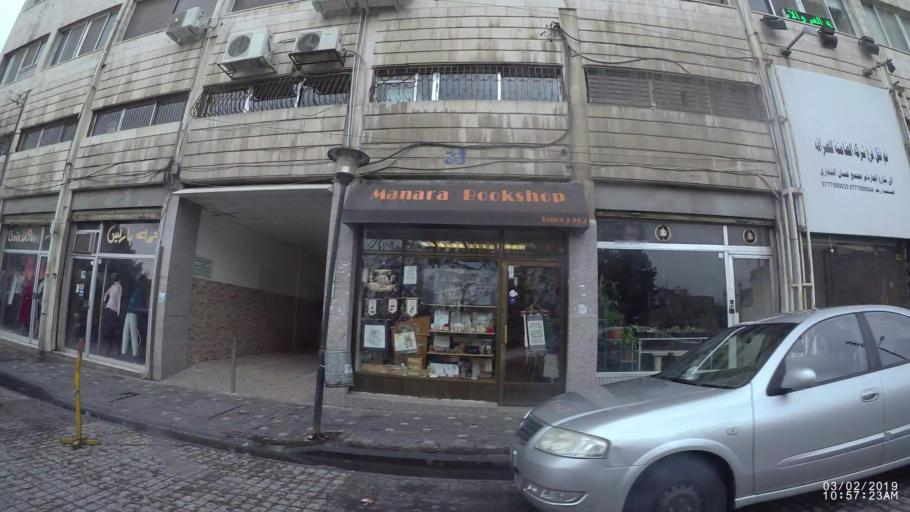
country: JO
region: Amman
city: Amman
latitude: 31.9493
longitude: 35.9269
